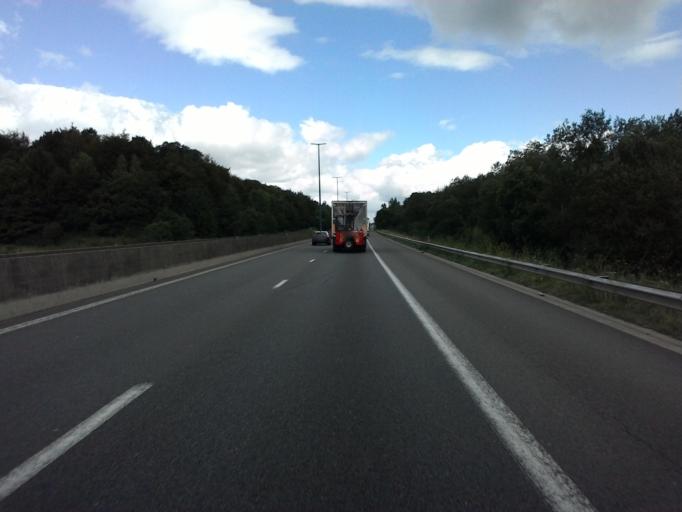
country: BE
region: Wallonia
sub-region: Province du Luxembourg
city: Habay-la-Vieille
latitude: 49.7319
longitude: 5.5794
